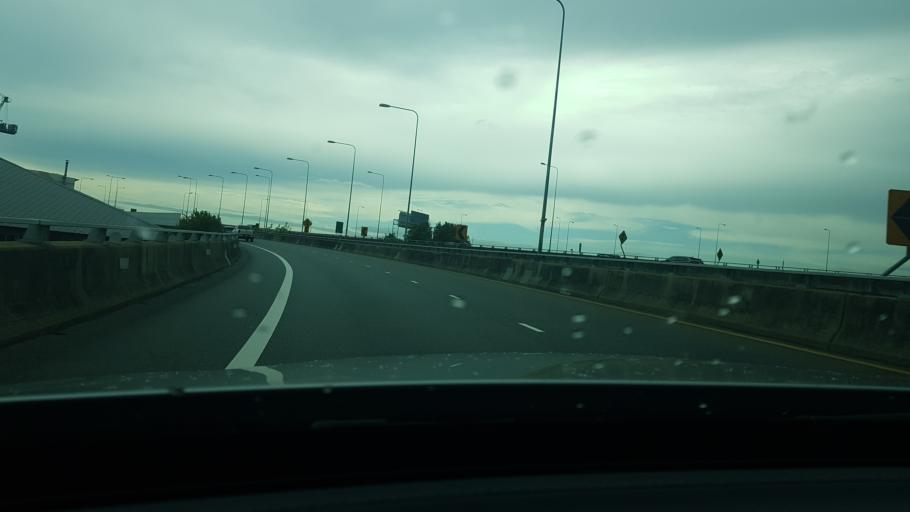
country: TH
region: Bangkok
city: Ratchathewi
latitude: 13.7707
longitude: 100.5308
